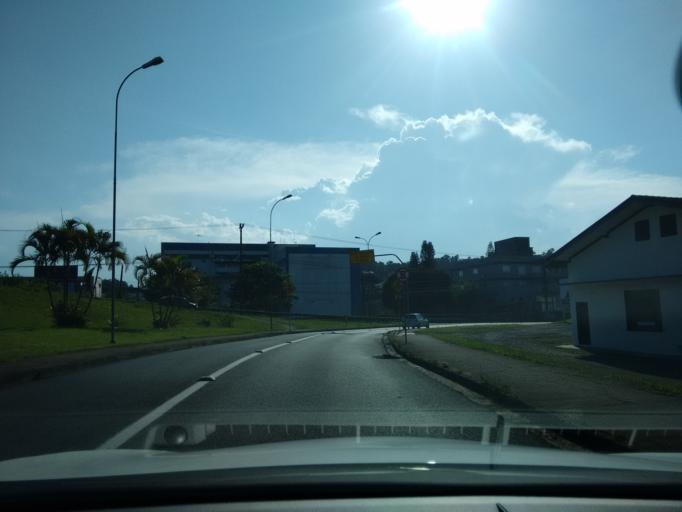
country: BR
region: Santa Catarina
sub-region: Blumenau
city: Blumenau
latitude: -26.8984
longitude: -49.0771
